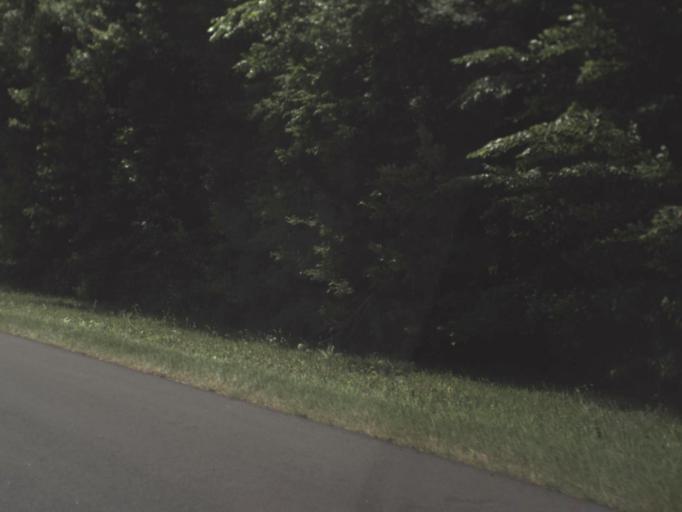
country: US
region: Florida
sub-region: Nassau County
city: Yulee
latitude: 30.6568
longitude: -81.6633
